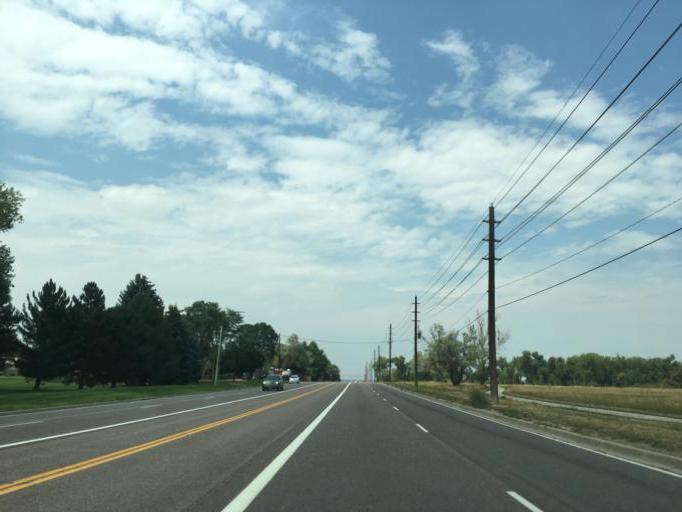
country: US
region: Colorado
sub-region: Jefferson County
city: Wheat Ridge
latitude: 39.7569
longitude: -105.1096
